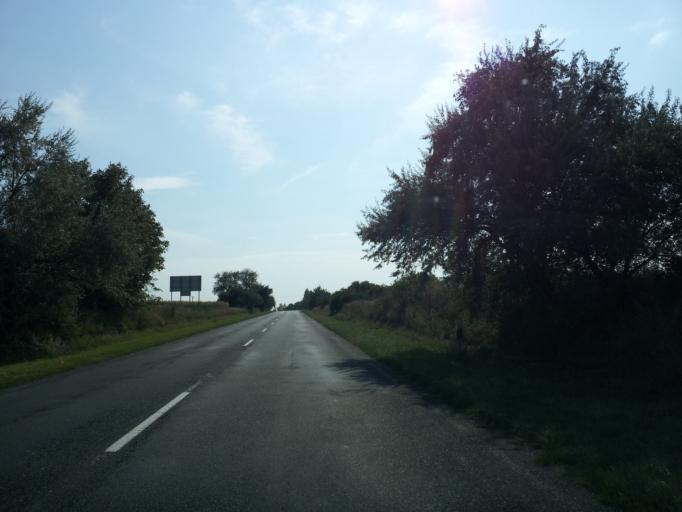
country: HU
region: Fejer
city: Lepseny
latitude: 46.9751
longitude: 18.2094
